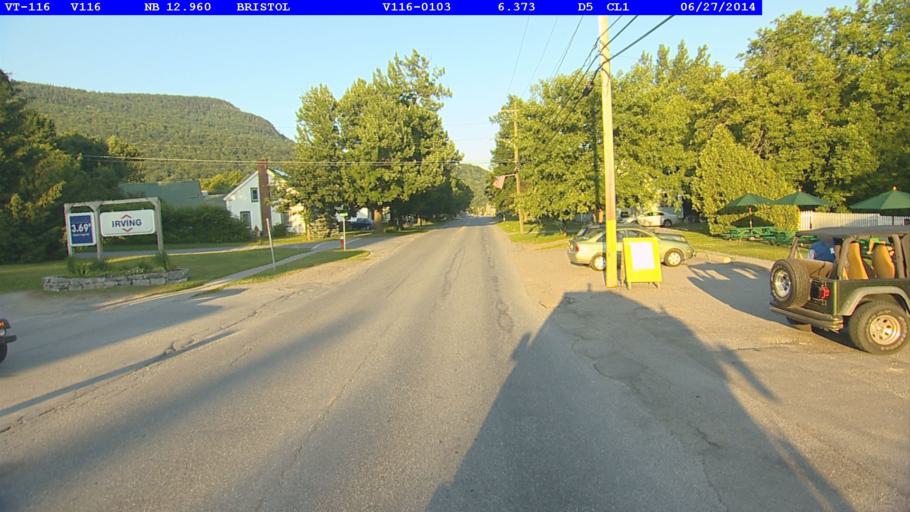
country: US
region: Vermont
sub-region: Addison County
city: Bristol
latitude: 44.1341
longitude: -73.0837
